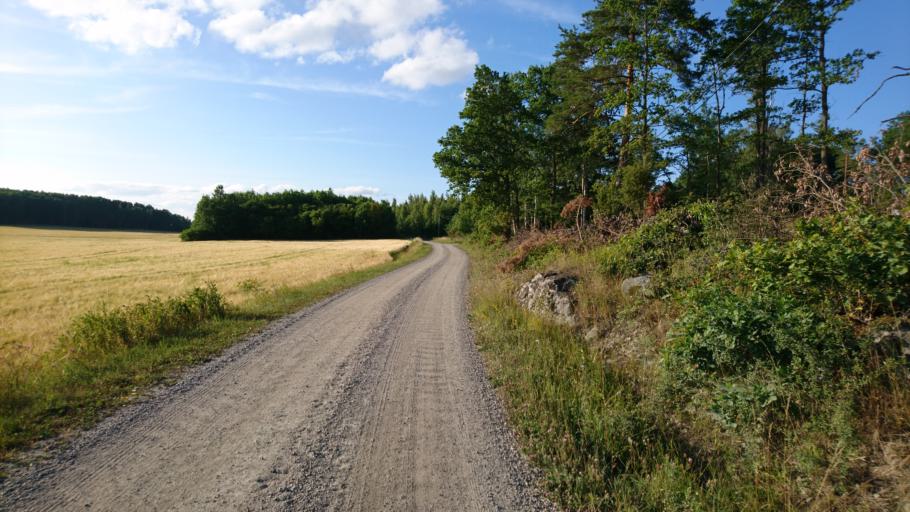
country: SE
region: Soedermanland
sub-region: Strangnas Kommun
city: Stallarholmen
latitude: 59.3904
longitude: 17.3050
